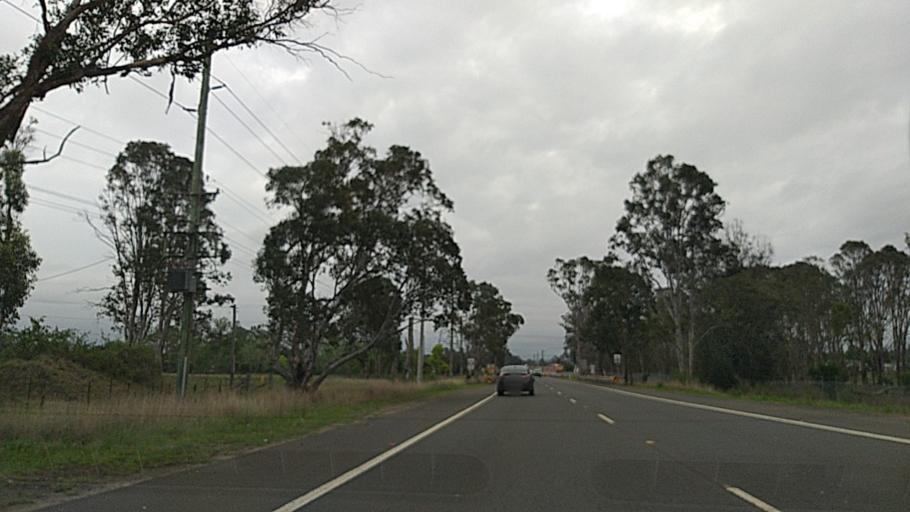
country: AU
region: New South Wales
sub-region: Penrith Municipality
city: Glenmore Park
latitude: -33.8000
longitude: 150.6977
